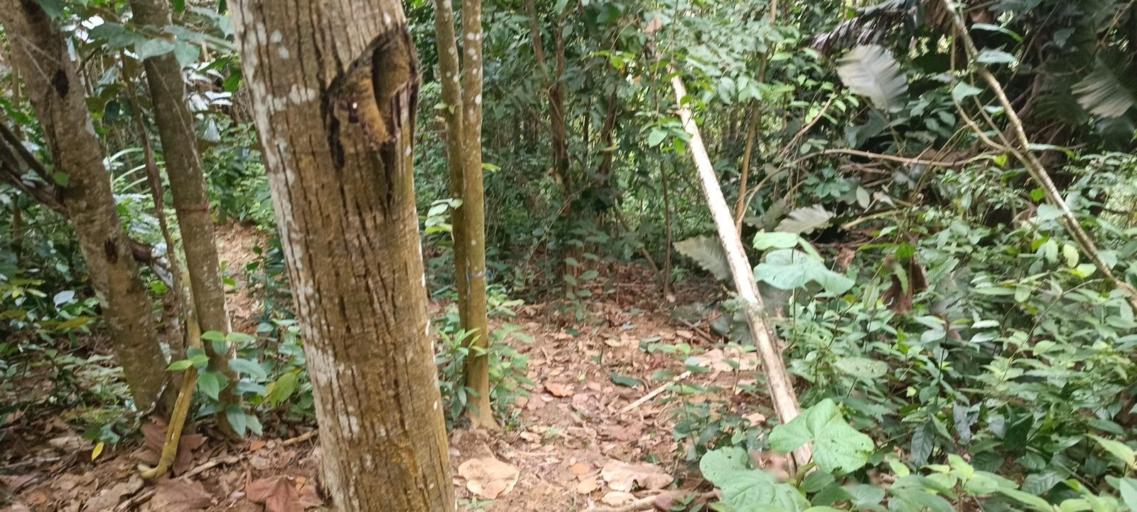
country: MY
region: Penang
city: Bukit Mertajam
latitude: 5.3539
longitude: 100.4966
